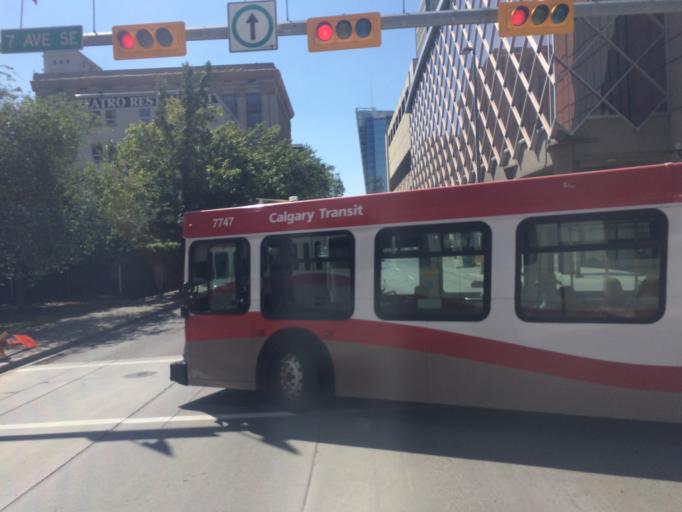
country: CA
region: Alberta
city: Calgary
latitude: 51.0464
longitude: -114.0600
